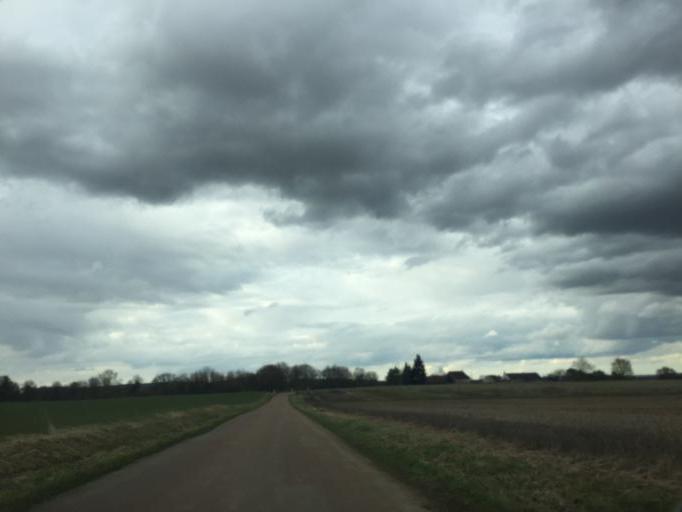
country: FR
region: Bourgogne
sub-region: Departement de l'Yonne
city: Fontenailles
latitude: 47.4893
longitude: 3.3753
